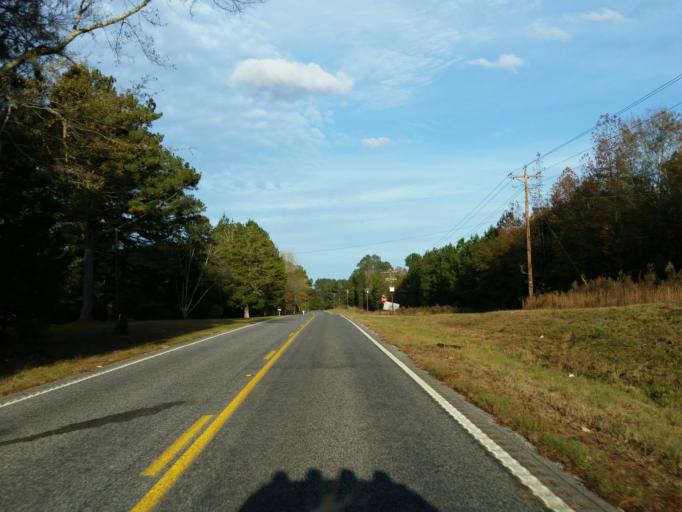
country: US
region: Mississippi
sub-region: Clarke County
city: Stonewall
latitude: 32.2172
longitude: -88.7805
